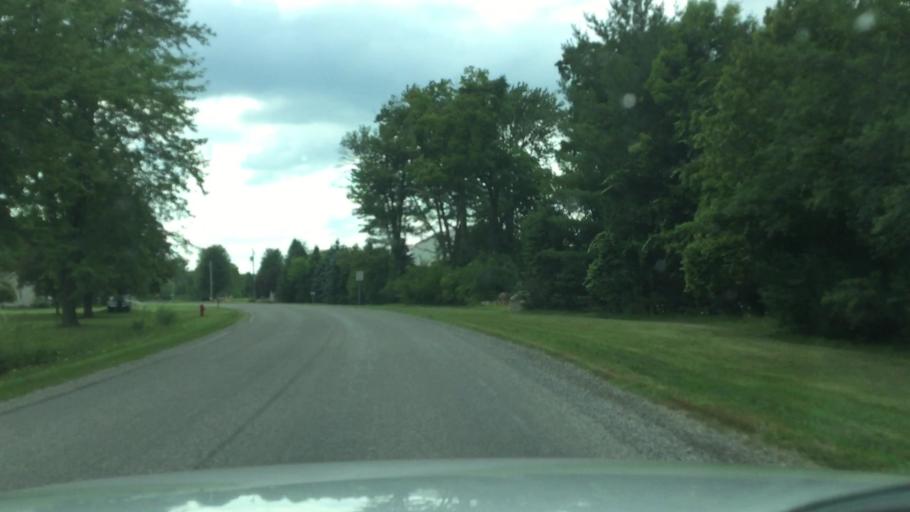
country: US
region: Michigan
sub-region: Saginaw County
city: Frankenmuth
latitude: 43.3216
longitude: -83.8076
